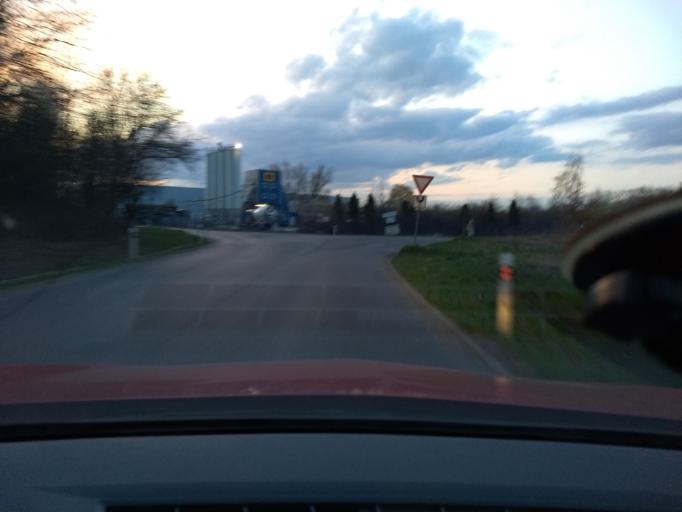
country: CZ
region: Central Bohemia
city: Hostivice
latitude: 50.0630
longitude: 14.2377
